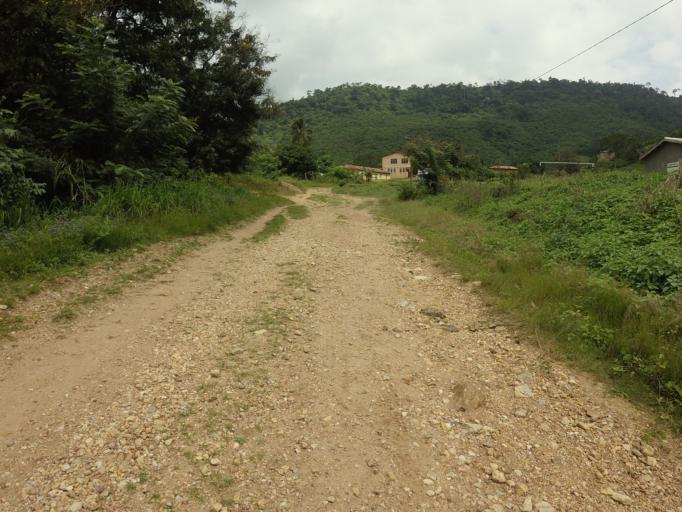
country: TG
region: Plateaux
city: Kpalime
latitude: 6.8581
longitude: 0.4409
